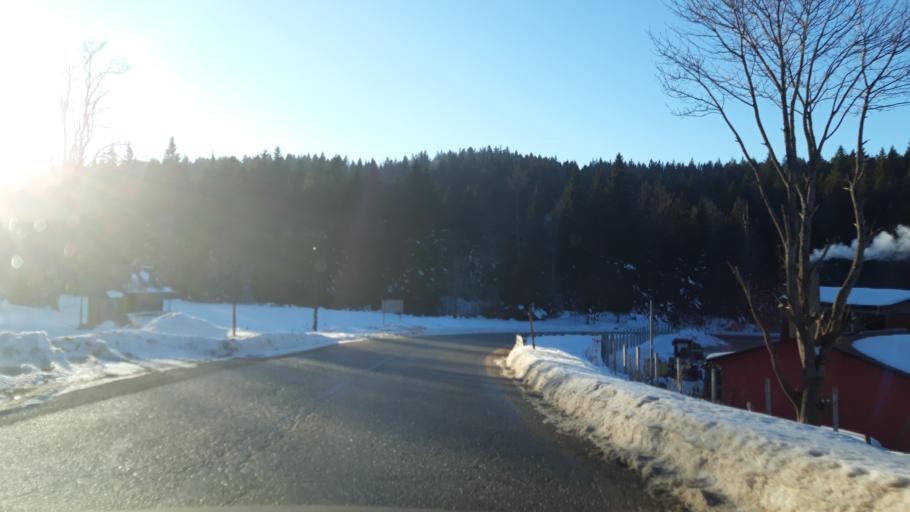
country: BA
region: Republika Srpska
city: Vlasenica
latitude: 44.1452
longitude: 18.9410
